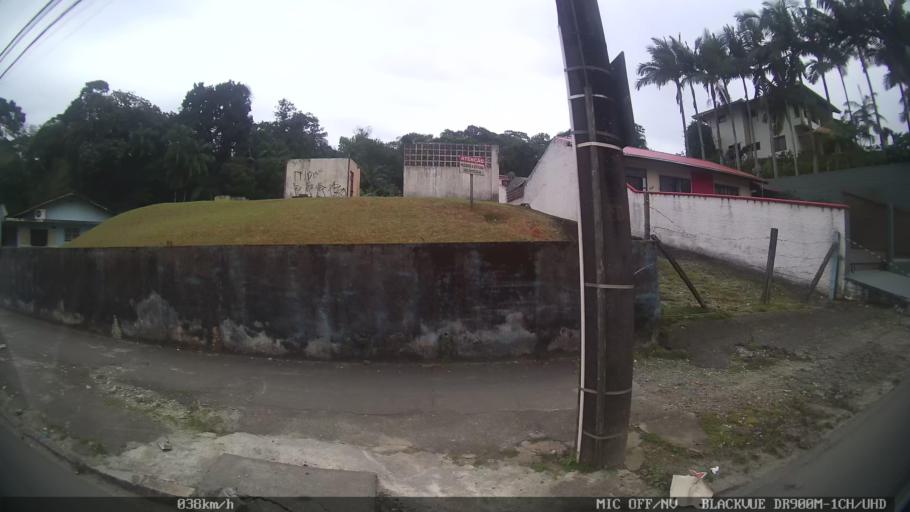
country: BR
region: Santa Catarina
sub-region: Joinville
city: Joinville
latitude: -26.2753
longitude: -48.8656
